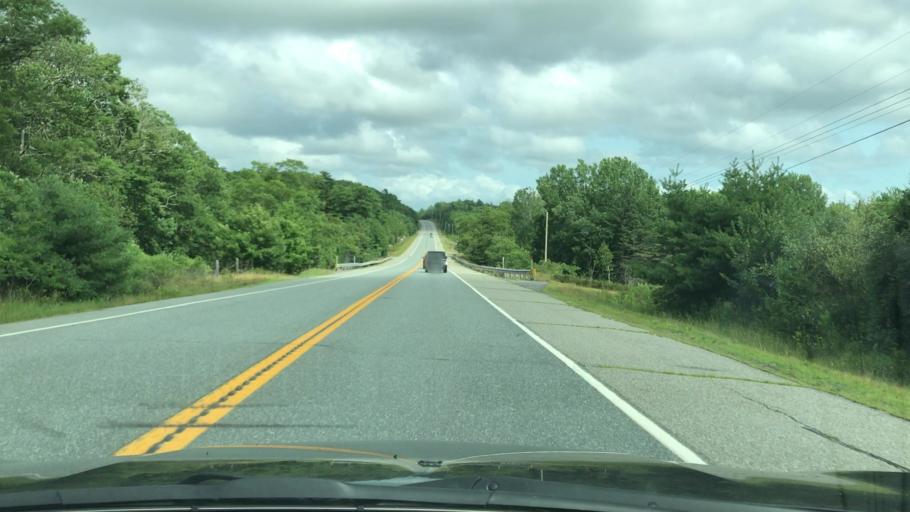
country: US
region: Maine
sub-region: Hancock County
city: Orland
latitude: 44.5663
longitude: -68.6137
